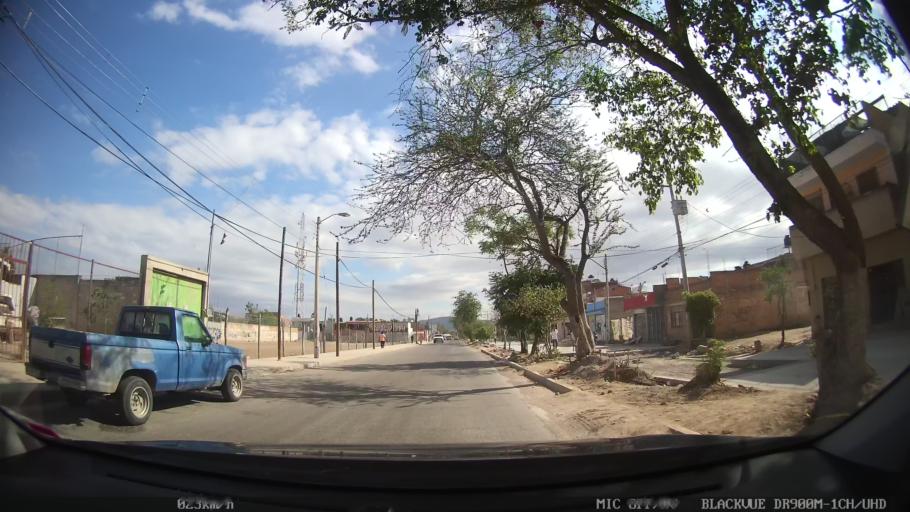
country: MX
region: Jalisco
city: Tonala
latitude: 20.6558
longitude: -103.2511
